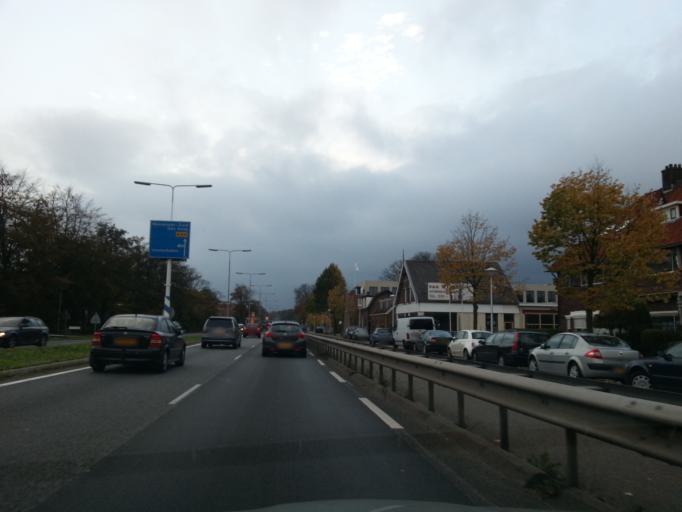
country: NL
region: South Holland
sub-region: Gemeente Wassenaar
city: Wassenaar
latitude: 52.1409
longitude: 4.4130
